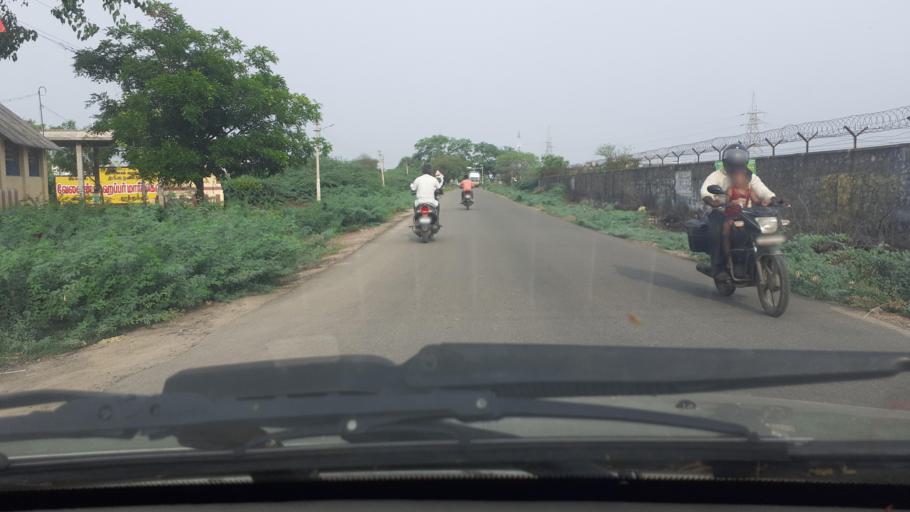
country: IN
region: Tamil Nadu
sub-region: Thoothukkudi
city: Korampallam
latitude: 8.7941
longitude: 78.1070
